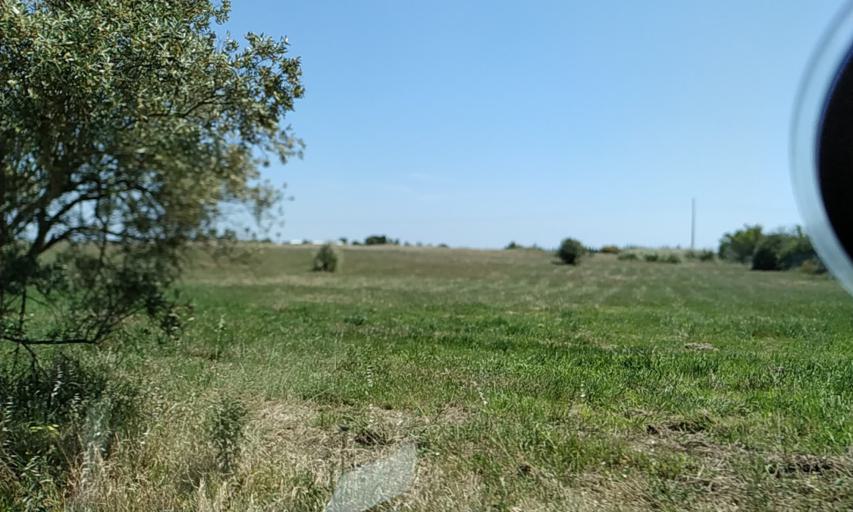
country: PT
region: Setubal
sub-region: Palmela
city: Palmela
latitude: 38.5924
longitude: -8.8440
